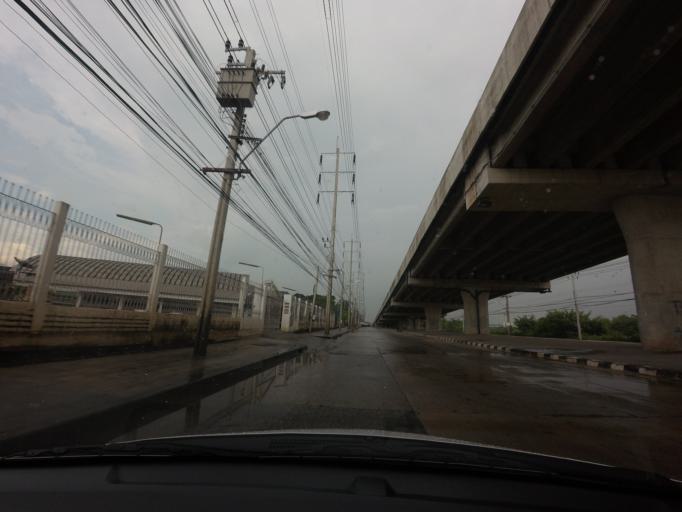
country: TH
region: Bangkok
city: Min Buri
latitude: 13.8154
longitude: 100.7522
